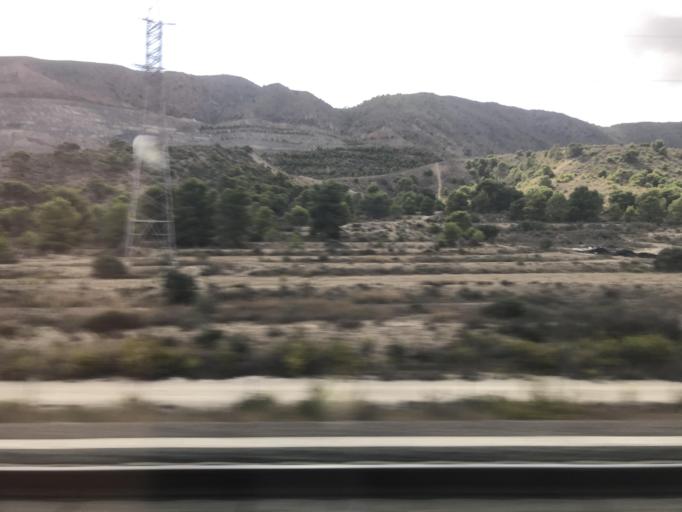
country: ES
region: Valencia
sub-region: Provincia de Alicante
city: San Vicent del Raspeig
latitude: 38.3672
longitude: -0.5827
